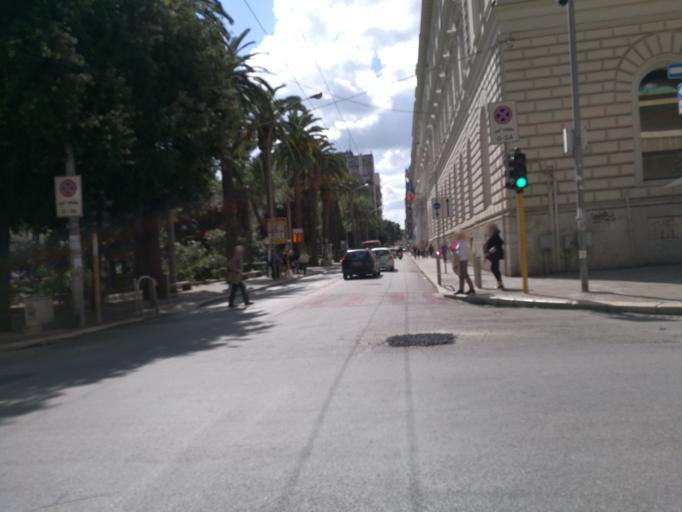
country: IT
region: Apulia
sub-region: Provincia di Bari
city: Bari
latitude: 41.1215
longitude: 16.8690
